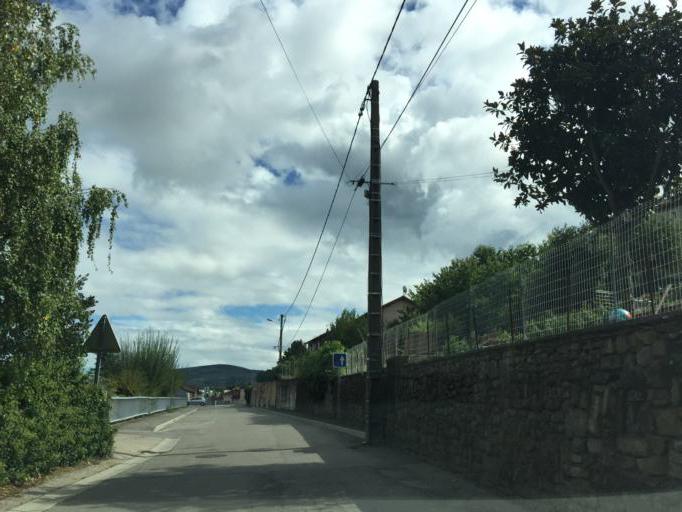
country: FR
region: Rhone-Alpes
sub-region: Departement de la Loire
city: Lorette
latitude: 45.5213
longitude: 4.5869
